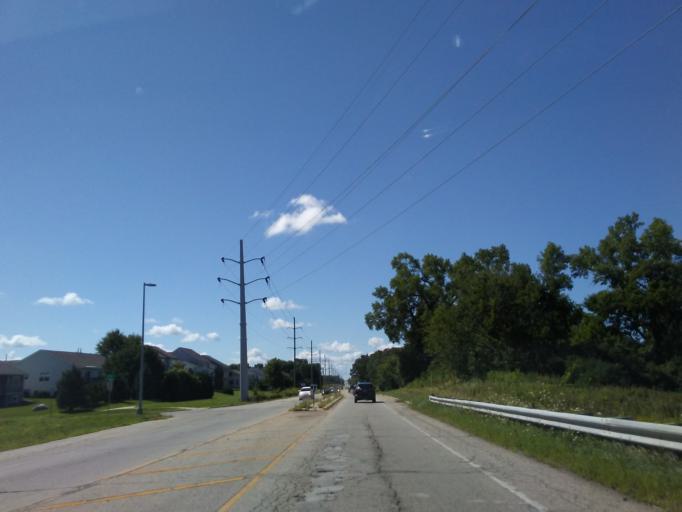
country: US
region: Wisconsin
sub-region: Dane County
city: Verona
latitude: 43.0298
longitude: -89.5333
